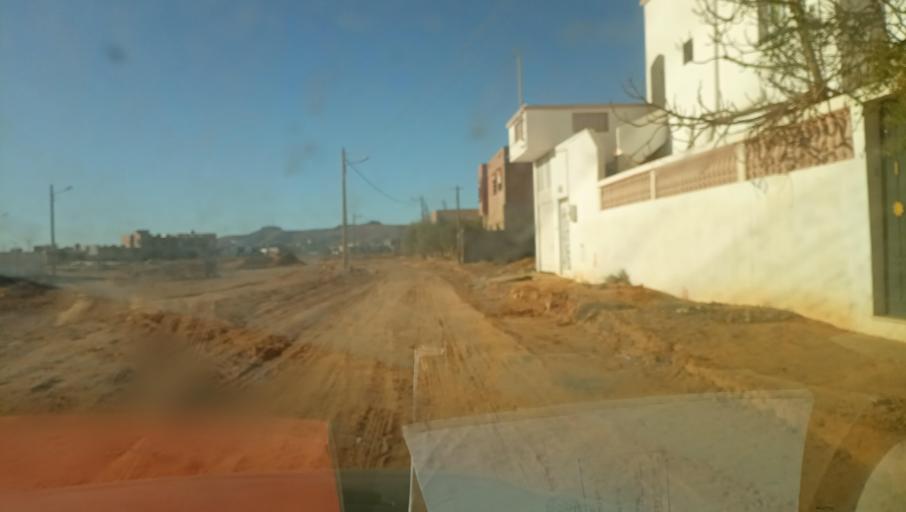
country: TN
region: Tataouine
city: Tataouine
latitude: 32.9864
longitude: 10.4596
